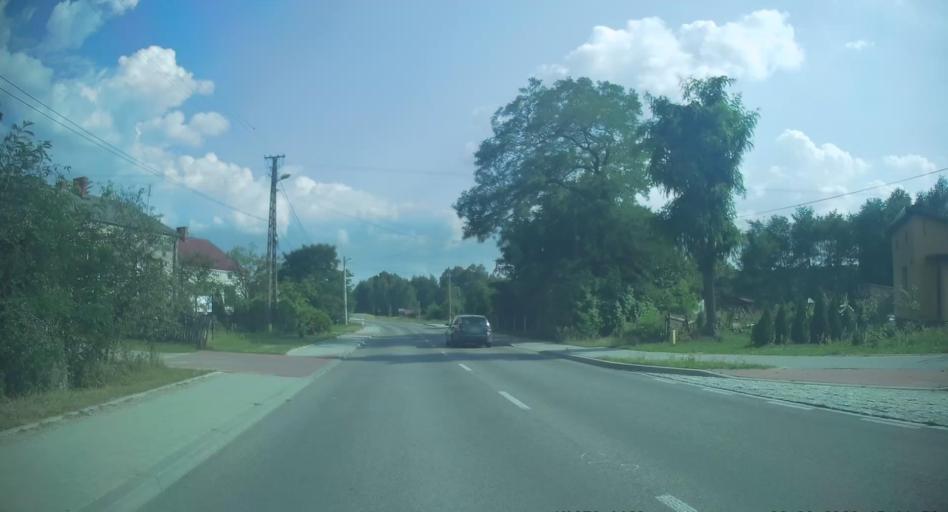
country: PL
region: Swietokrzyskie
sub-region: Powiat konecki
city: Radoszyce
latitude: 51.0625
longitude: 20.2750
